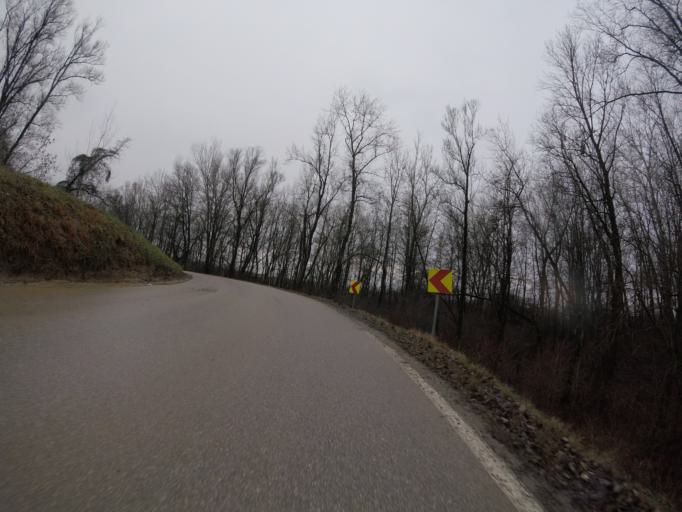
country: HR
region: Zagrebacka
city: Kuce
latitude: 45.6989
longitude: 16.2122
